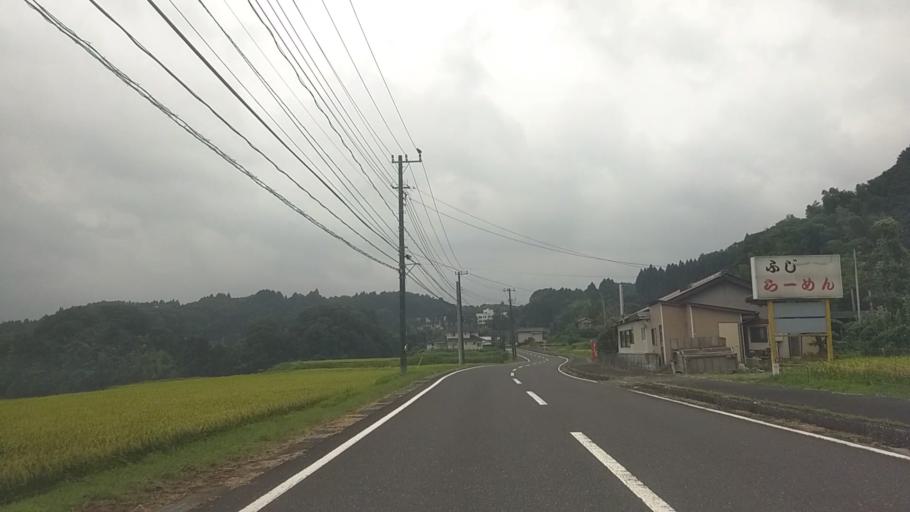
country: JP
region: Chiba
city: Kawaguchi
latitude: 35.2579
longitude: 140.0562
